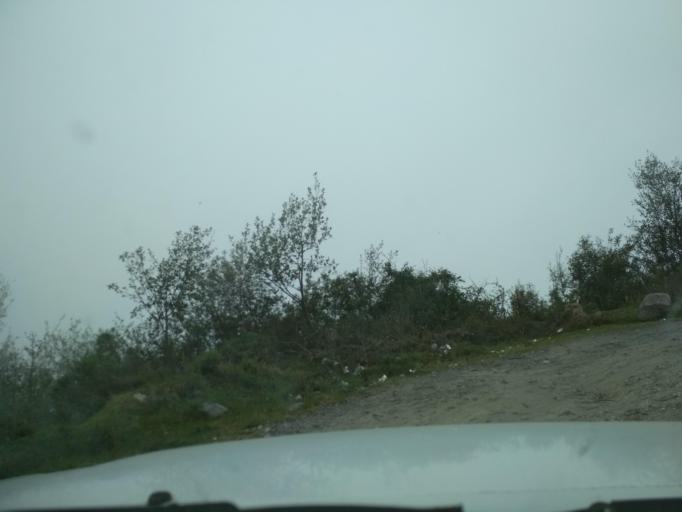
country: MX
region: Veracruz
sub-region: La Perla
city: Chilapa
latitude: 18.9818
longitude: -97.1926
